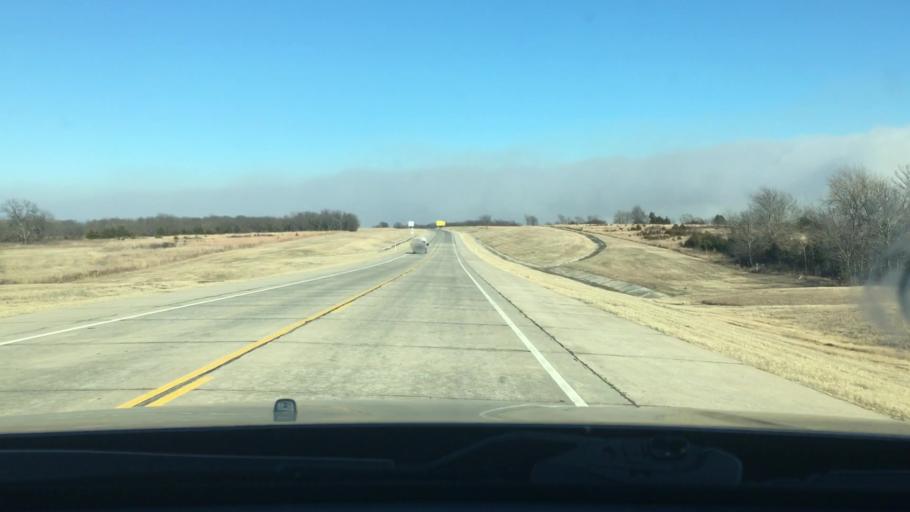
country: US
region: Oklahoma
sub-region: Murray County
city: Sulphur
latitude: 34.5484
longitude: -96.9501
